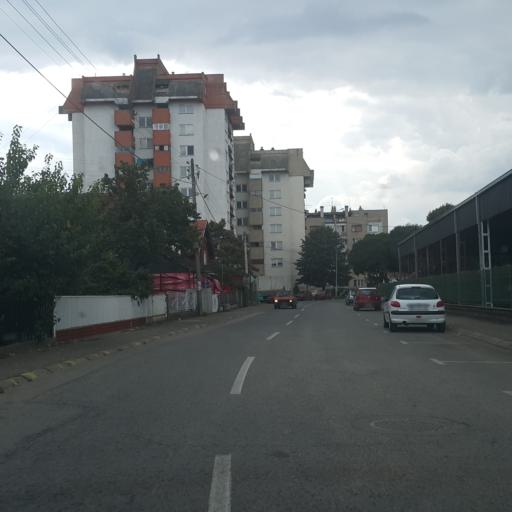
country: RS
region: Central Serbia
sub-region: Zajecarski Okrug
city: Knjazevac
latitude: 43.5717
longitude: 22.2588
